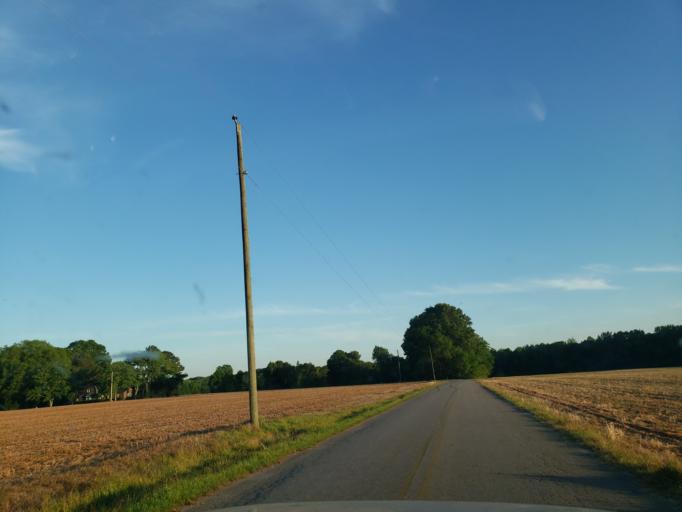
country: US
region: Alabama
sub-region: Madison County
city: Hazel Green
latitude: 34.9451
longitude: -86.5355
